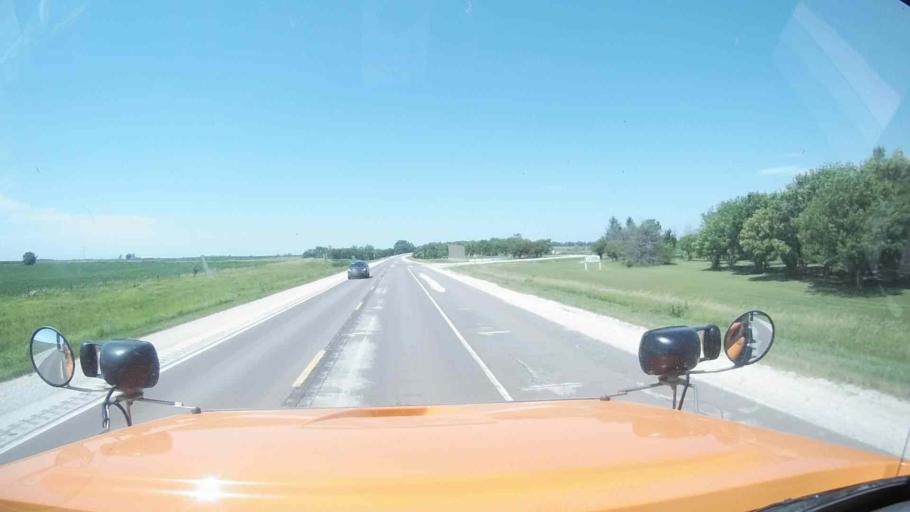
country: US
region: Iowa
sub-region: Greene County
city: Jefferson
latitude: 42.0331
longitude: -94.2063
